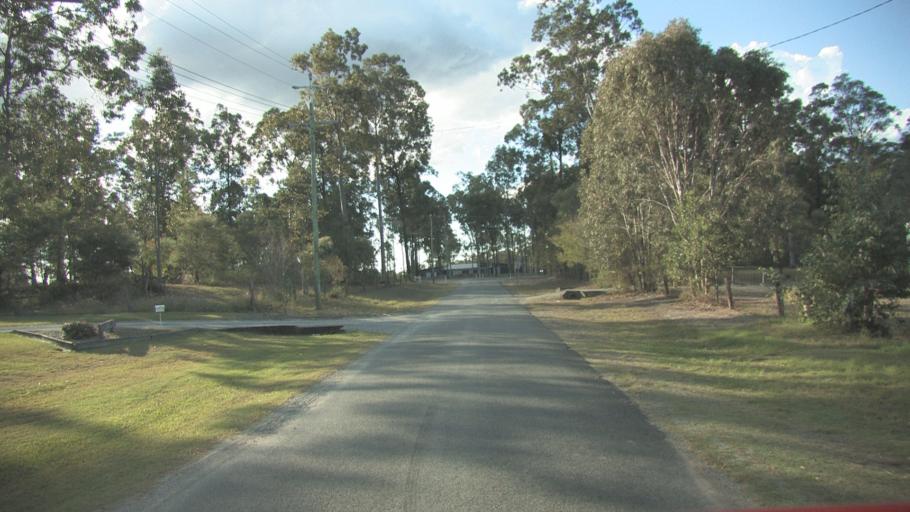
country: AU
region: Queensland
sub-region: Ipswich
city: Springfield Lakes
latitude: -27.6976
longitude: 152.9543
